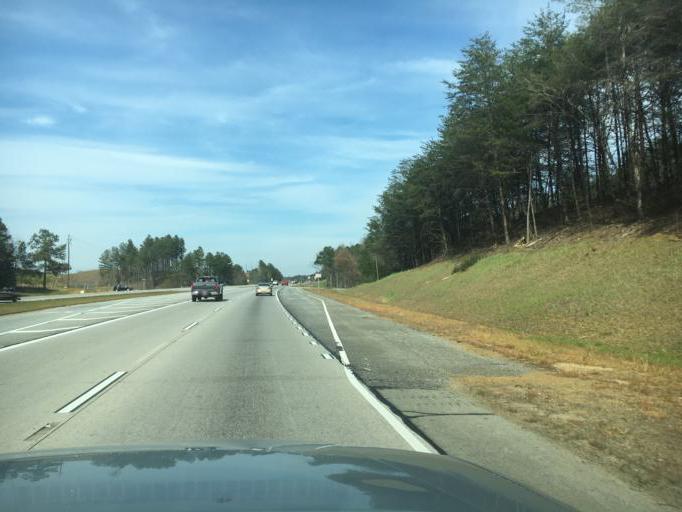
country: US
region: Georgia
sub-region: Hall County
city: Lula
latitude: 34.3642
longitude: -83.7411
